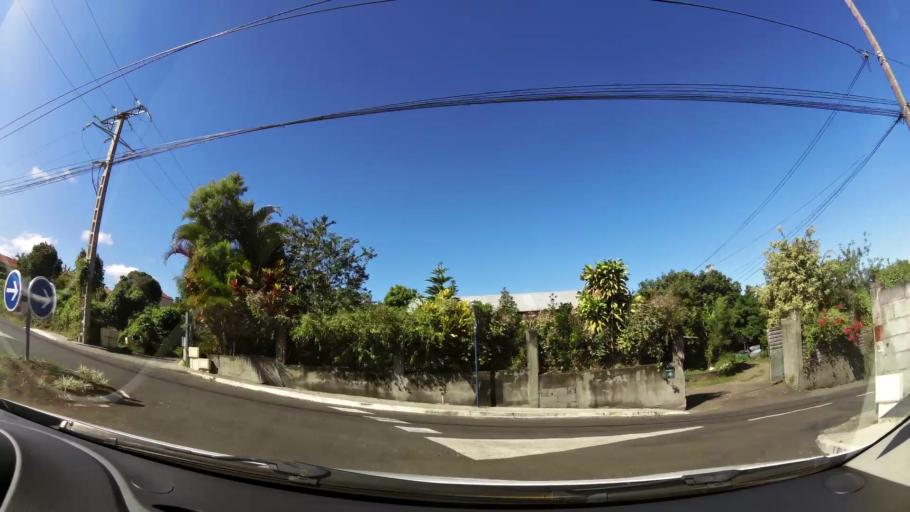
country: RE
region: Reunion
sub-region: Reunion
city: Le Tampon
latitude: -21.2704
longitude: 55.4984
